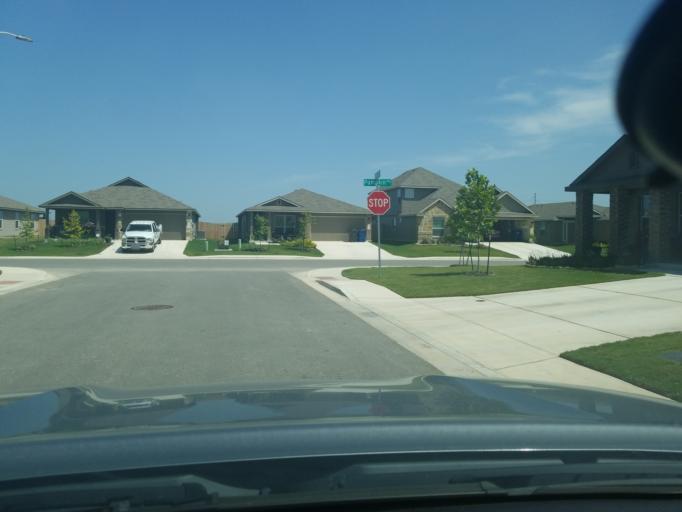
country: US
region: Texas
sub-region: Guadalupe County
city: Lake Dunlap
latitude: 29.6719
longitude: -98.0345
